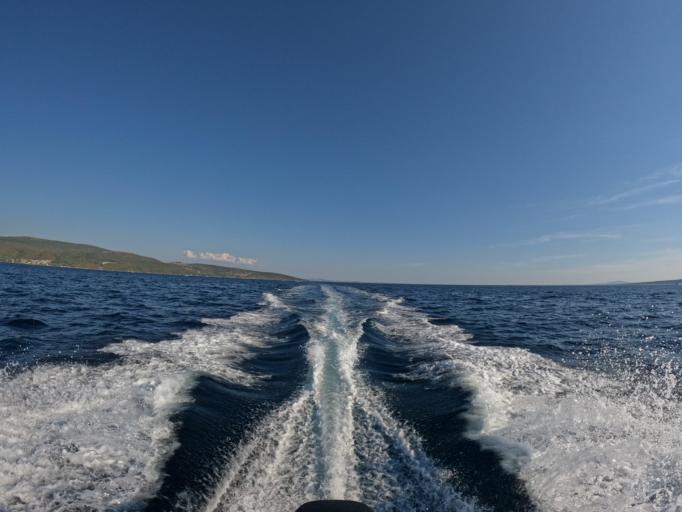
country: HR
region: Primorsko-Goranska
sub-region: Grad Krk
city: Krk
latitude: 45.0154
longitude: 14.5862
